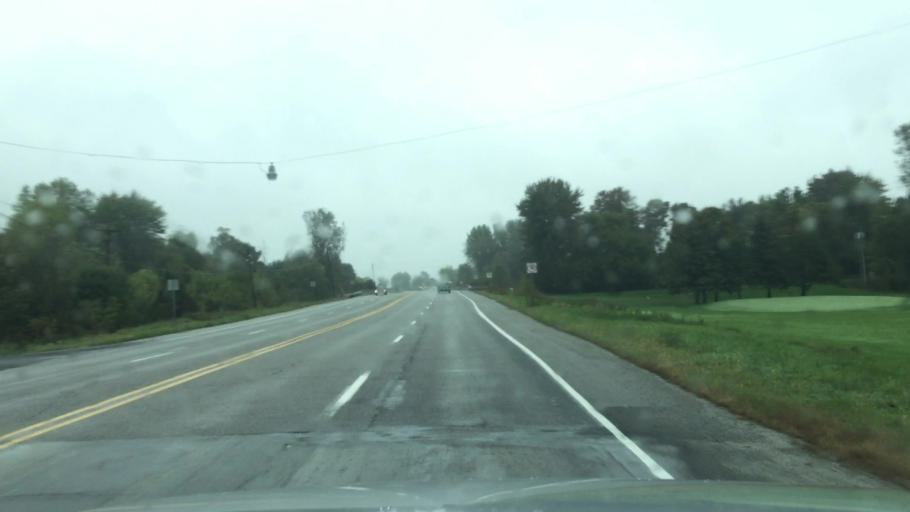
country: US
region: Michigan
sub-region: Saginaw County
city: Bridgeport
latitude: 43.3287
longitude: -83.8287
